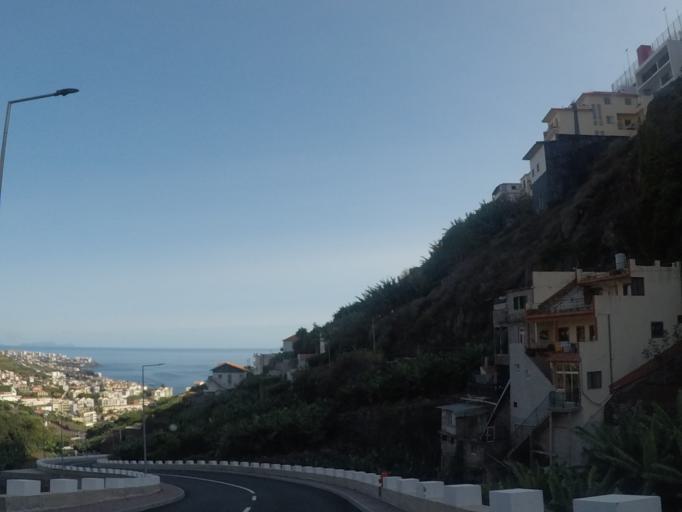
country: PT
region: Madeira
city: Camara de Lobos
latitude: 32.6565
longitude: -16.9905
